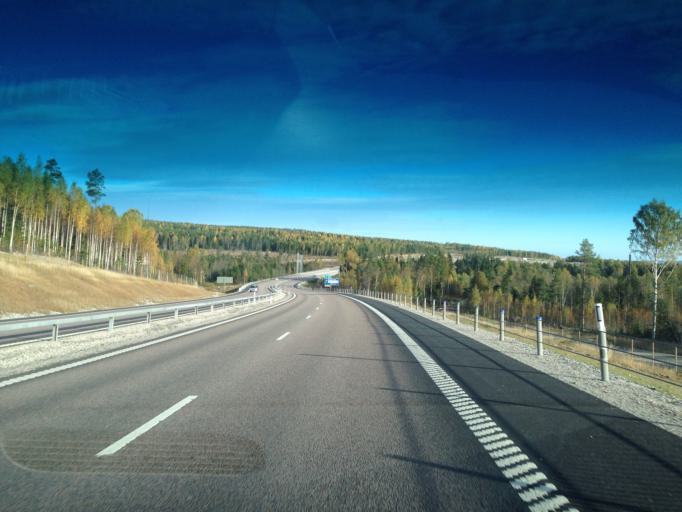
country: SE
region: Vaesternorrland
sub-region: Sundsvalls Kommun
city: Stockvik
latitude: 62.3287
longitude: 17.3462
